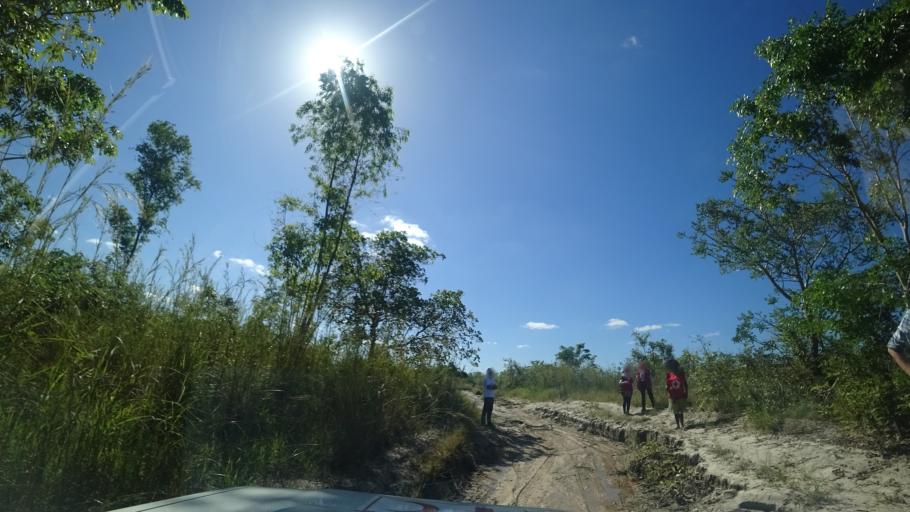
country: MZ
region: Sofala
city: Dondo
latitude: -19.4749
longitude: 34.6298
